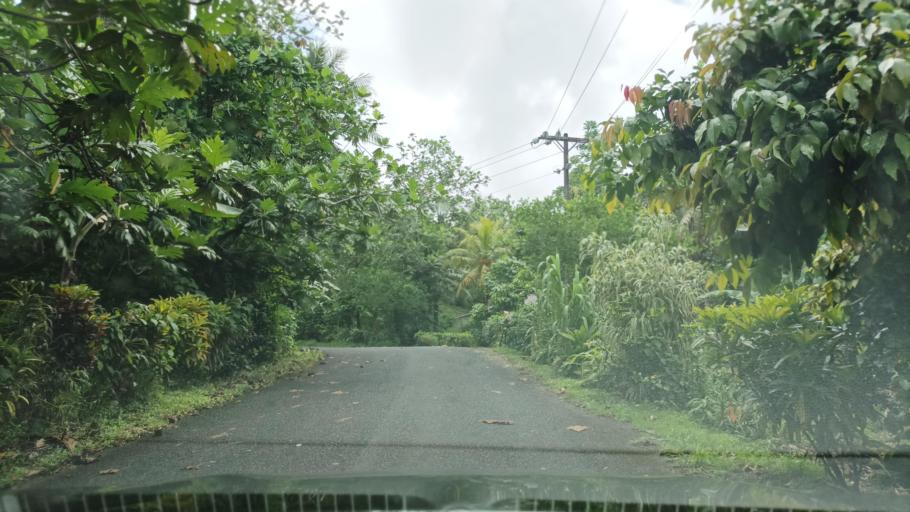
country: FM
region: Pohnpei
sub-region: Madolenihm Municipality
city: Madolenihm Municipality Government
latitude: 6.8441
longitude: 158.3012
